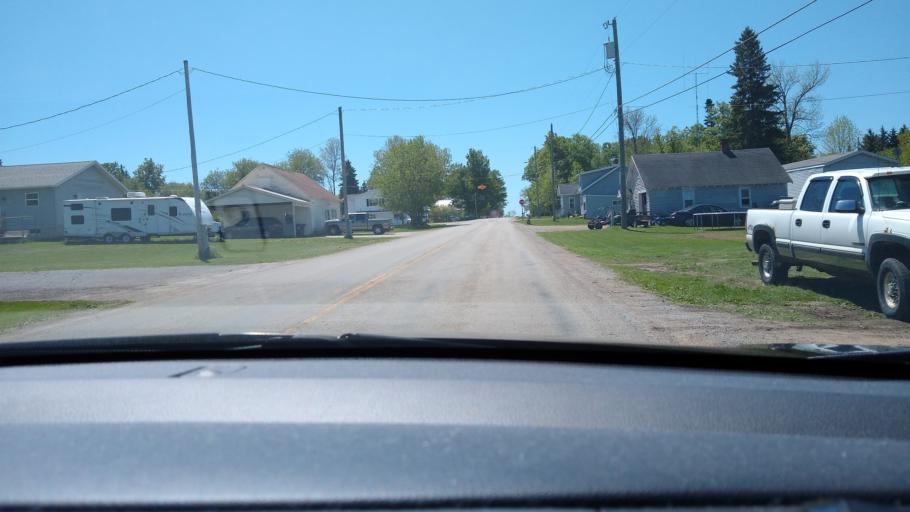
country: US
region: Michigan
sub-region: Delta County
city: Escanaba
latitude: 45.8271
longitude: -87.1831
